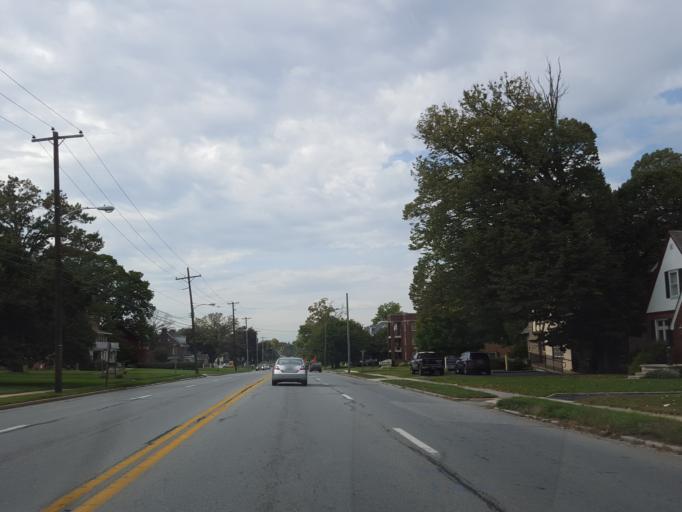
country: US
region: Pennsylvania
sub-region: York County
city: East York
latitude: 39.9738
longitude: -76.6846
